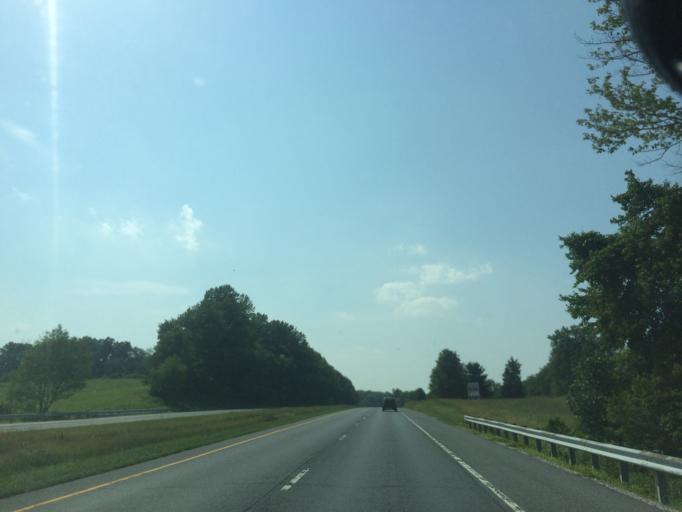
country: US
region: Maryland
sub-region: Howard County
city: Columbia
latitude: 39.2916
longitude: -76.8930
